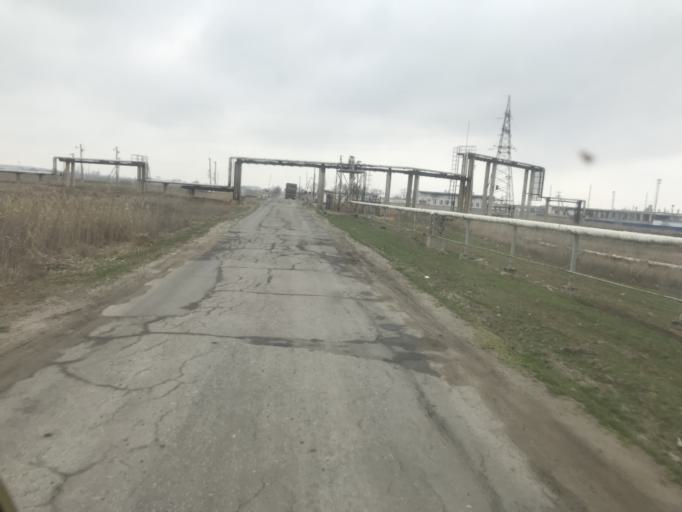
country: RU
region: Volgograd
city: Svetlyy Yar
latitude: 48.5133
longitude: 44.6347
